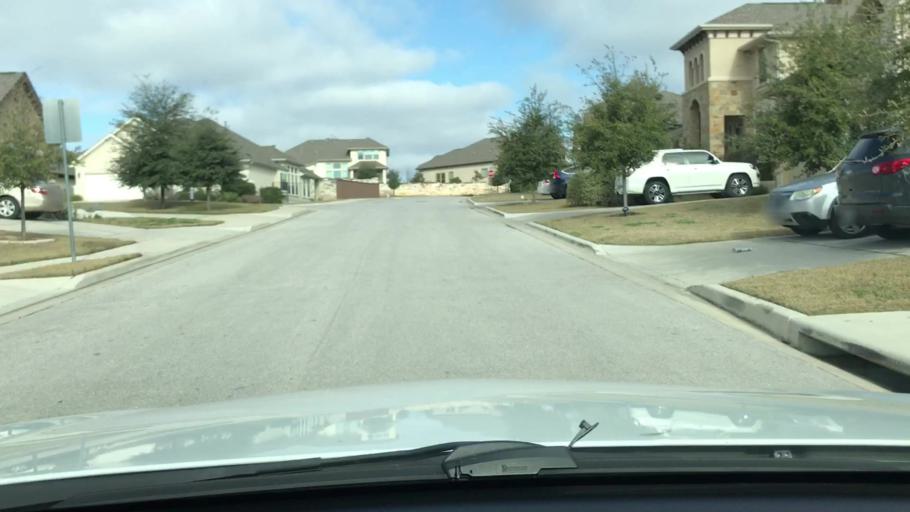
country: US
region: Texas
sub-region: Travis County
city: Bee Cave
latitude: 30.3147
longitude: -97.9588
